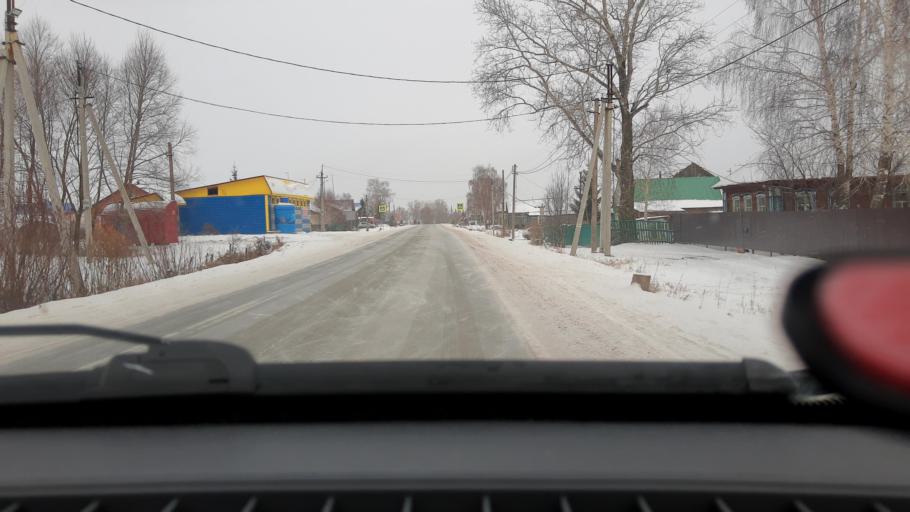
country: RU
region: Bashkortostan
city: Iglino
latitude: 54.7359
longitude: 56.3966
